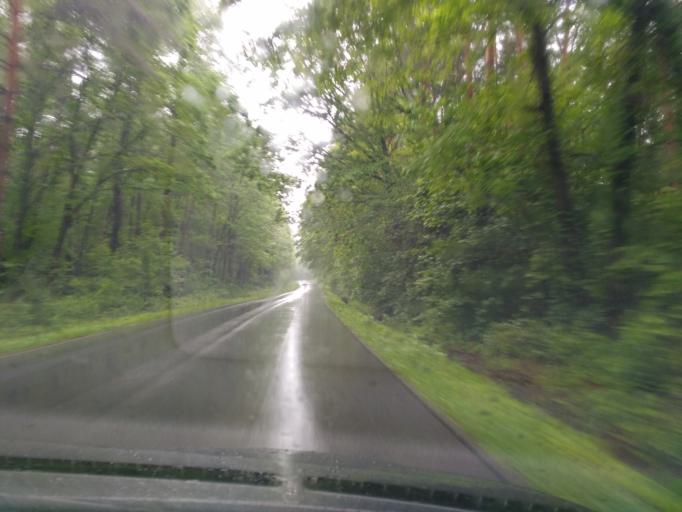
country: PL
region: Subcarpathian Voivodeship
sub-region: Powiat jasielski
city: Debowiec
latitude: 49.6624
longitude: 21.4353
